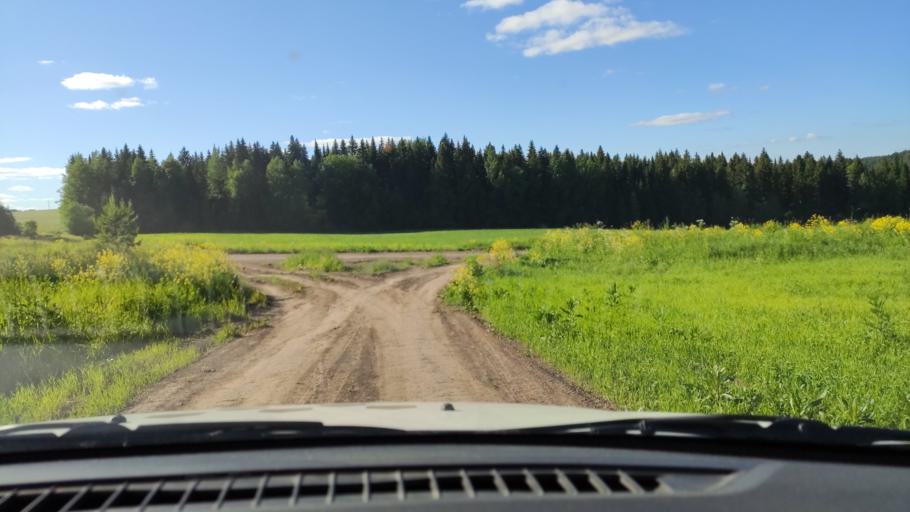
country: RU
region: Perm
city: Orda
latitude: 57.3002
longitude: 56.5900
